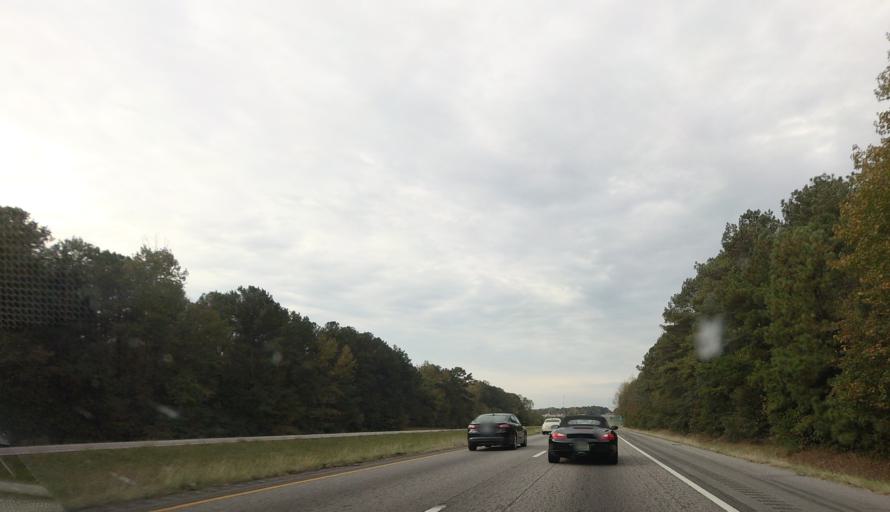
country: US
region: Alabama
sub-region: Lee County
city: Opelika
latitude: 32.6208
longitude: -85.3940
